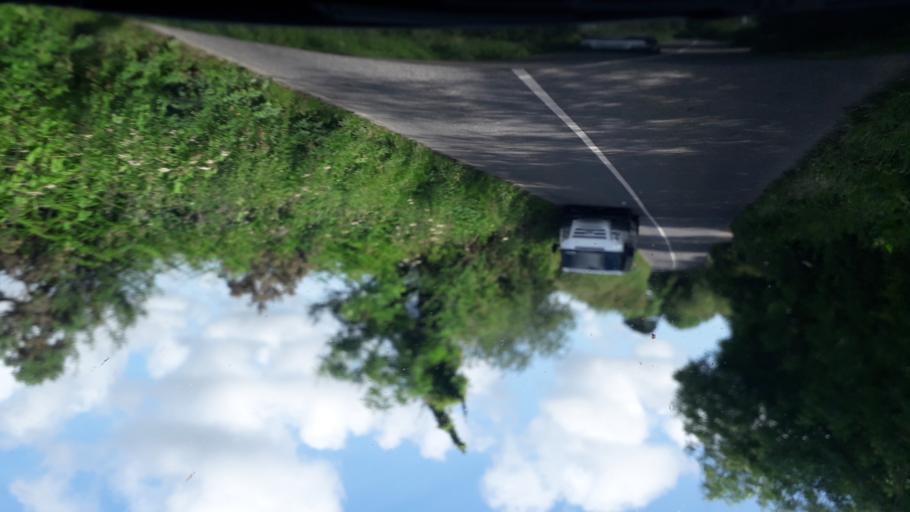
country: IE
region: Leinster
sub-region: Loch Garman
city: Loch Garman
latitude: 52.2703
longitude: -6.5509
